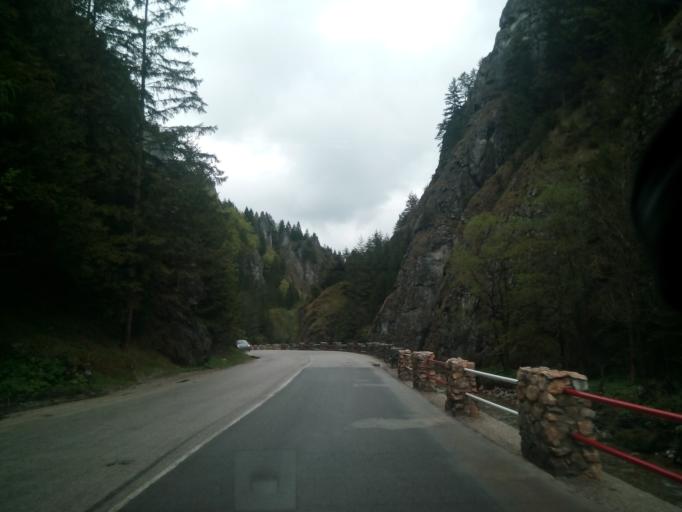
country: SK
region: Zilinsky
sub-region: Okres Zilina
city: Terchova
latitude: 49.2428
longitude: 19.0385
